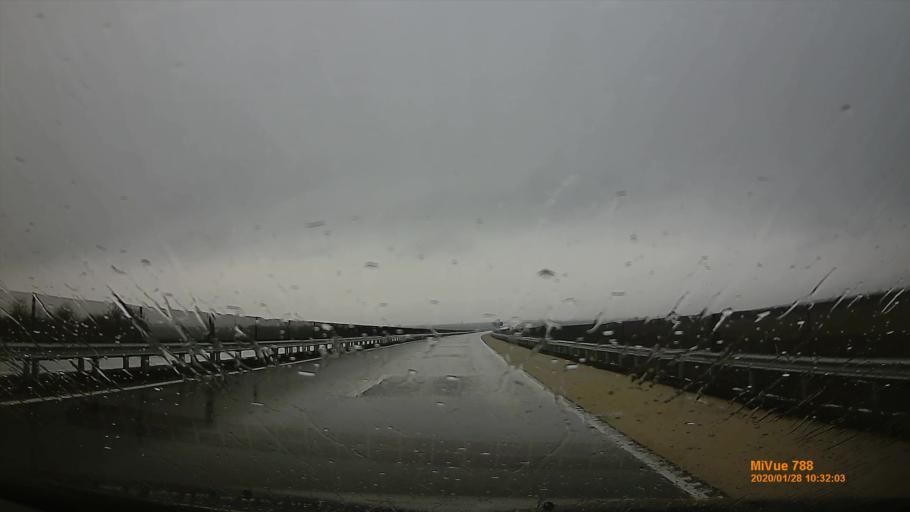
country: HU
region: Pest
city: Gomba
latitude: 47.3454
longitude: 19.4965
